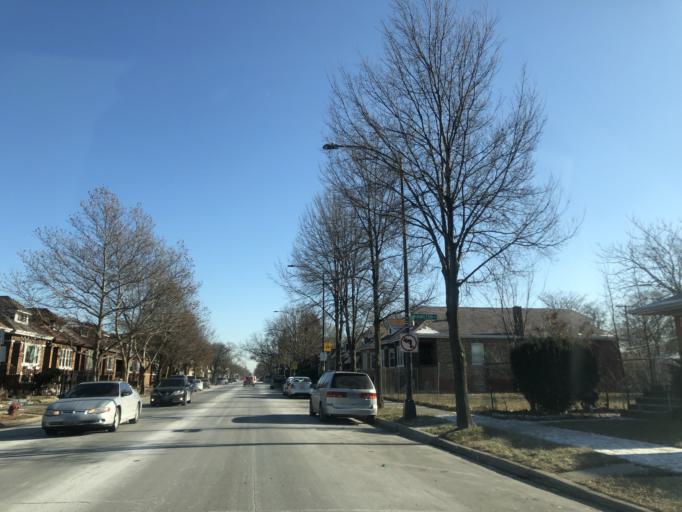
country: US
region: Illinois
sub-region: Cook County
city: Evergreen Park
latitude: 41.7648
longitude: -87.6775
